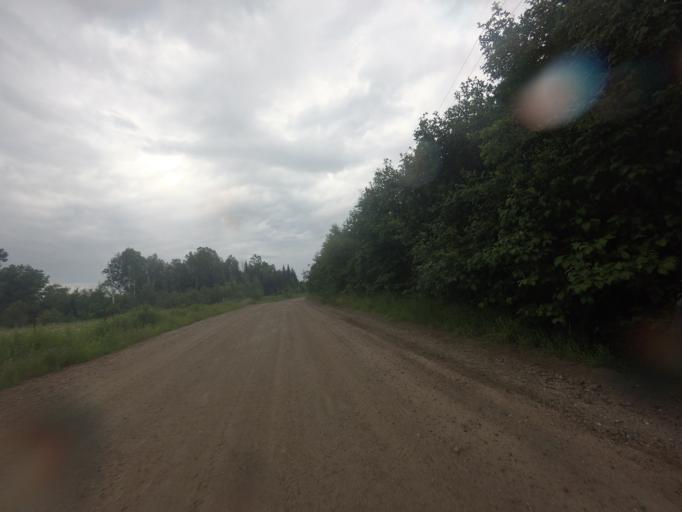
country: CA
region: Quebec
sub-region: Outaouais
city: Maniwaki
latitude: 46.4480
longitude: -75.9377
